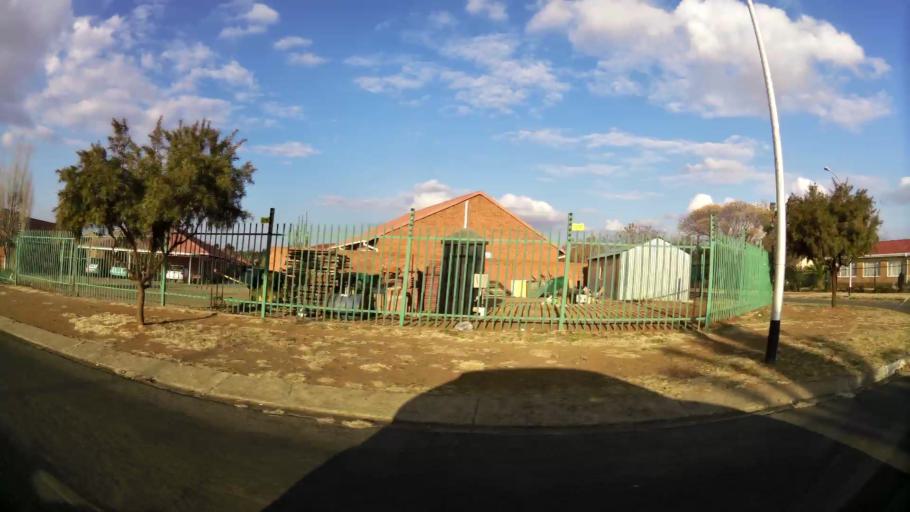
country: ZA
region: Orange Free State
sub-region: Mangaung Metropolitan Municipality
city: Bloemfontein
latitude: -29.1500
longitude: 26.1864
